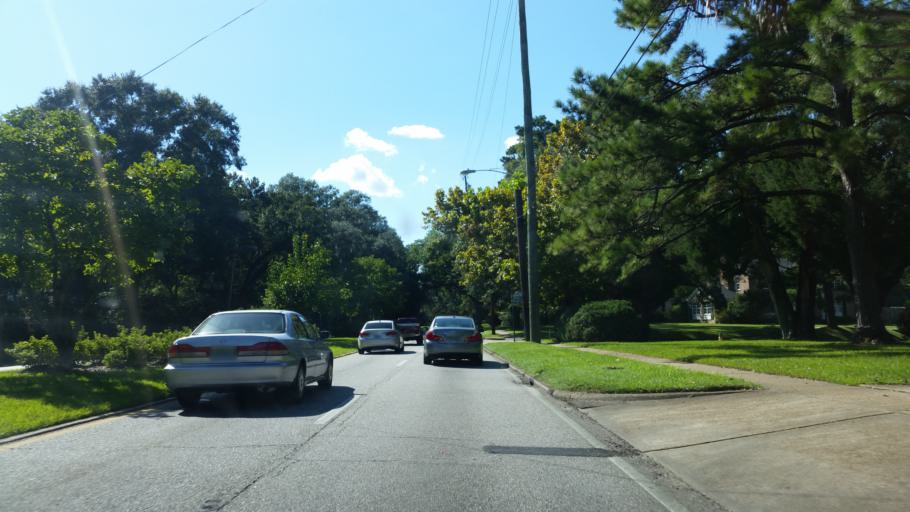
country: US
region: Alabama
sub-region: Mobile County
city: Prichard
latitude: 30.6931
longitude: -88.0943
